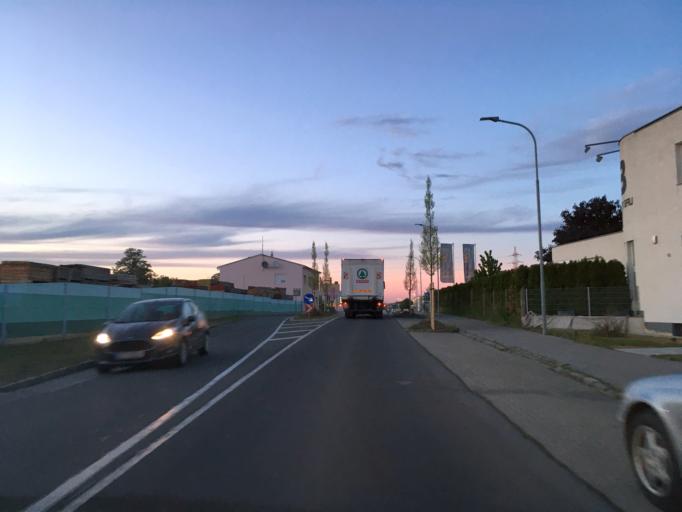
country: AT
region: Lower Austria
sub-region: Politischer Bezirk Wien-Umgebung
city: Zwolfaxing
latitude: 48.1200
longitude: 16.4689
